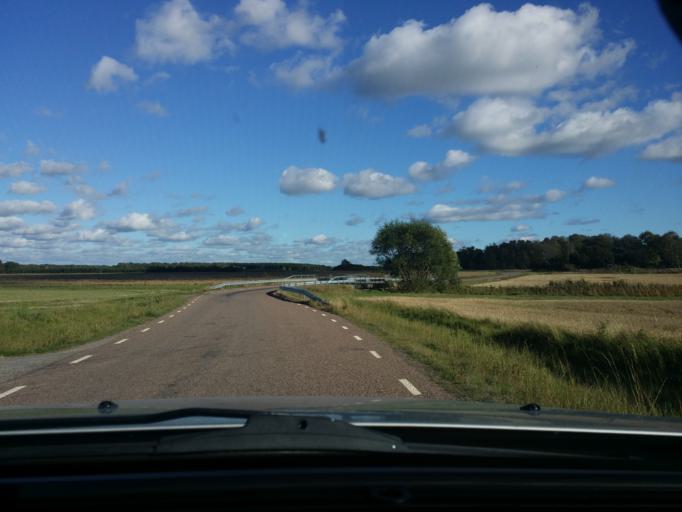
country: SE
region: Vaestmanland
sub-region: Vasteras
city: Vasteras
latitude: 59.5382
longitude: 16.4630
